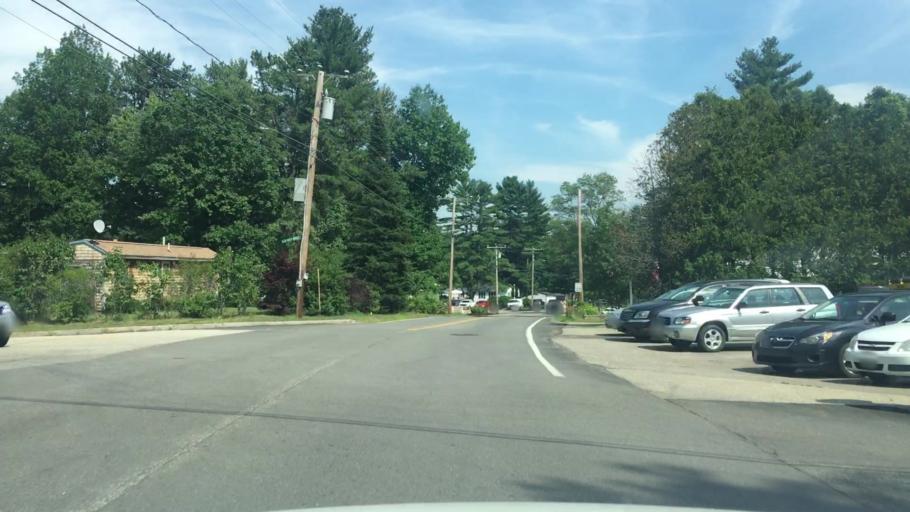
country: US
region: New Hampshire
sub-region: Strafford County
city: Rochester
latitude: 43.3422
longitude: -70.9670
